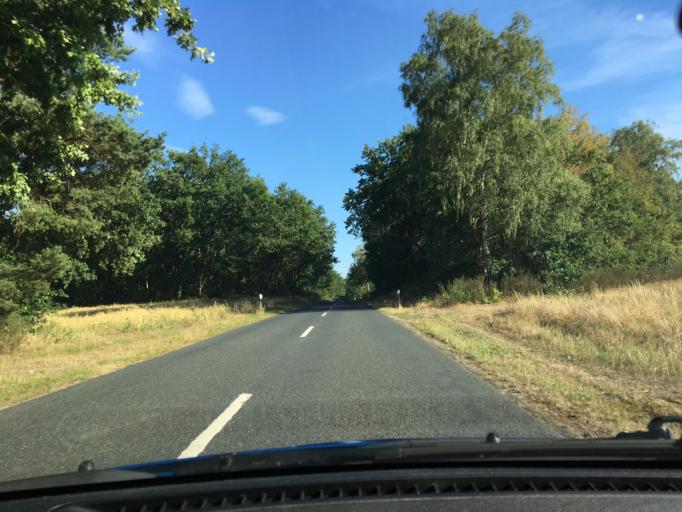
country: DE
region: Lower Saxony
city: Dahlenburg
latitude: 53.2033
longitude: 10.7123
